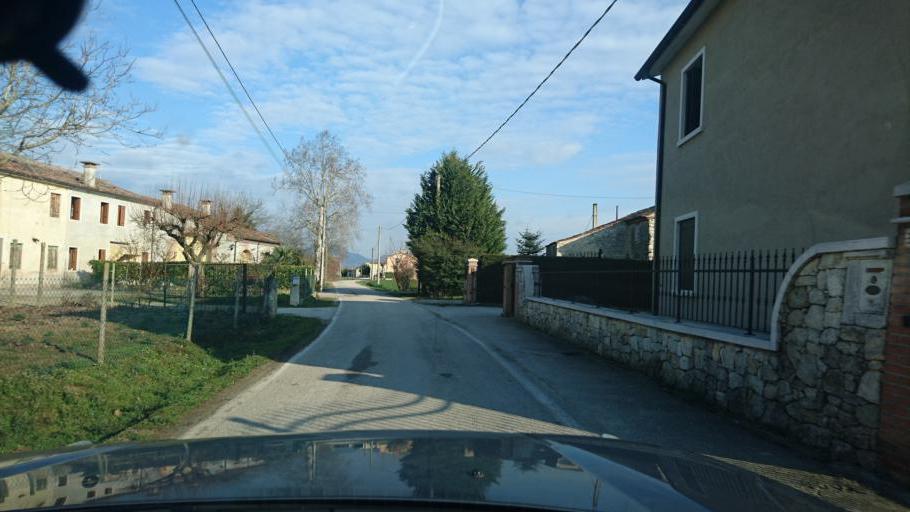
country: IT
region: Veneto
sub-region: Provincia di Vicenza
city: Sossano
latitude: 45.3555
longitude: 11.5308
